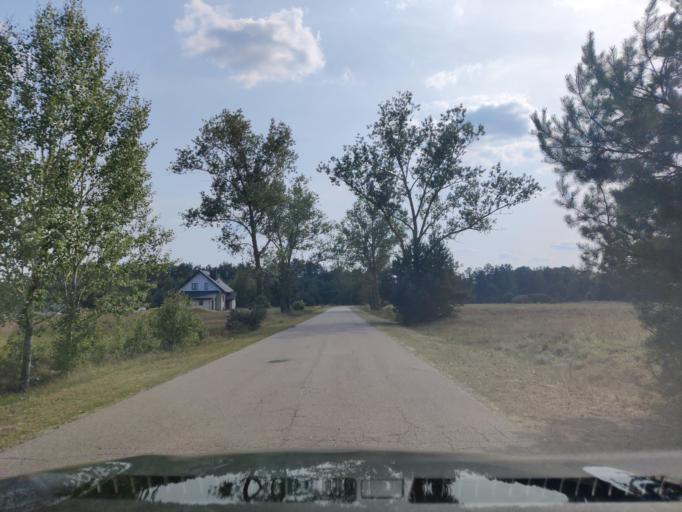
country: PL
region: Masovian Voivodeship
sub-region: Powiat wyszkowski
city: Rzasnik
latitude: 52.7690
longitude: 21.4589
